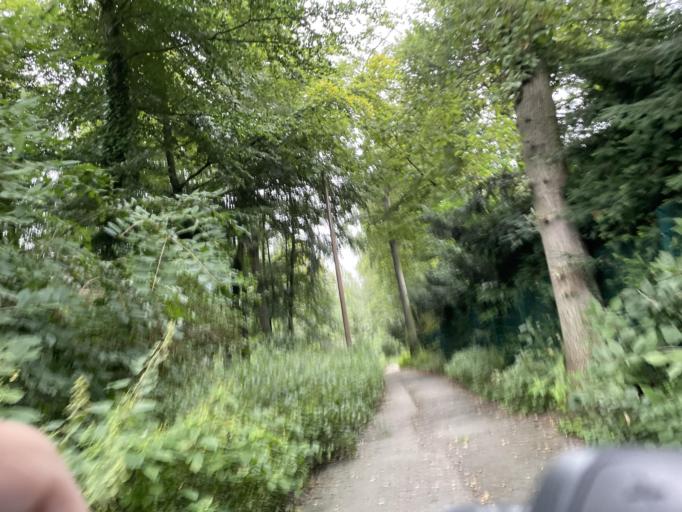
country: DE
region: North Rhine-Westphalia
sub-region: Regierungsbezirk Dusseldorf
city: Essen
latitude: 51.4210
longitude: 7.0465
